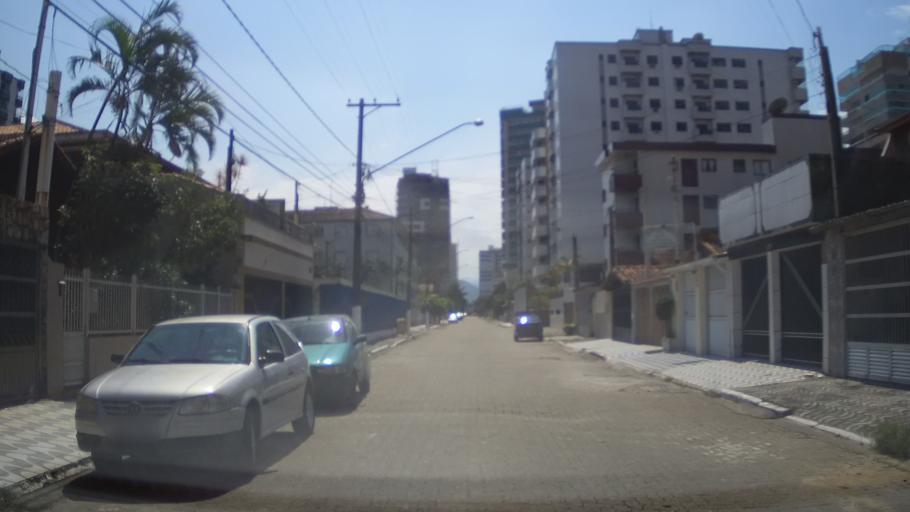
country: BR
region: Sao Paulo
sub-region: Praia Grande
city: Praia Grande
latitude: -24.0132
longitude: -46.4260
